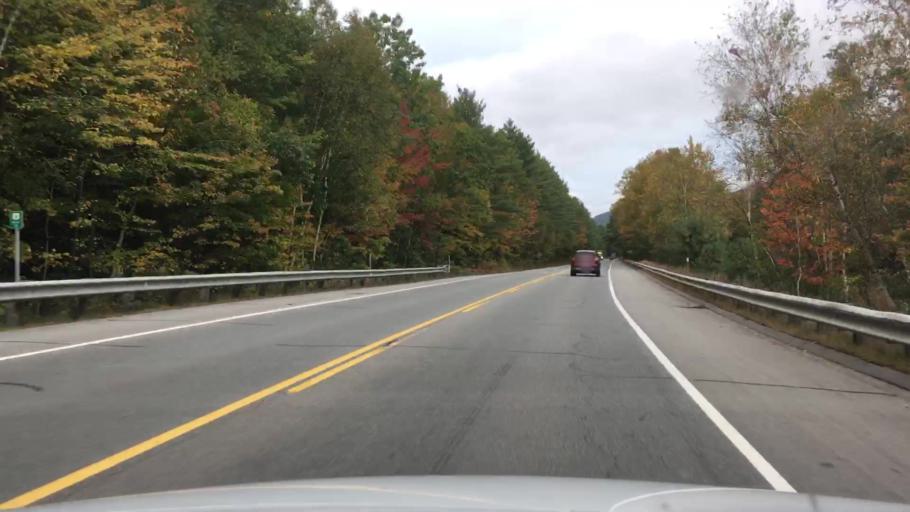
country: US
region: New Hampshire
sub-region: Coos County
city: Gorham
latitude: 44.3855
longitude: -71.0239
